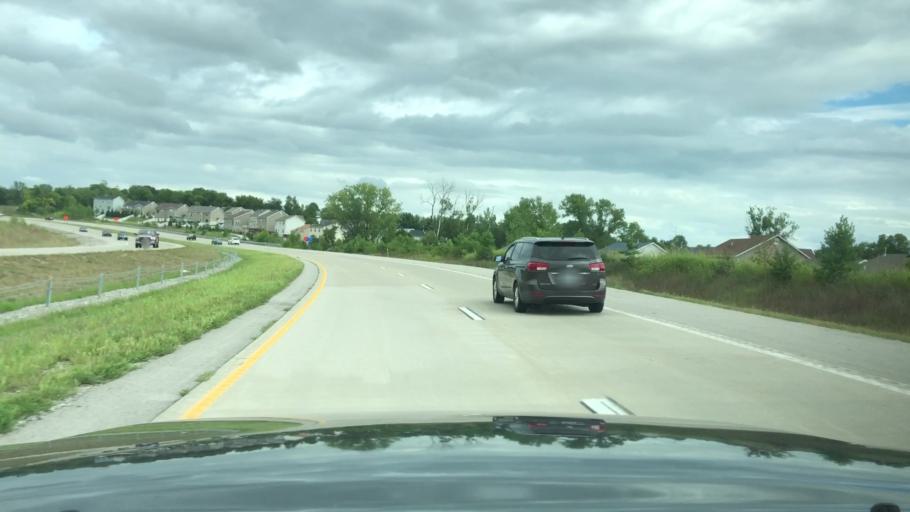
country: US
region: Missouri
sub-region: Saint Charles County
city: Cottleville
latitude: 38.7332
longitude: -90.6643
